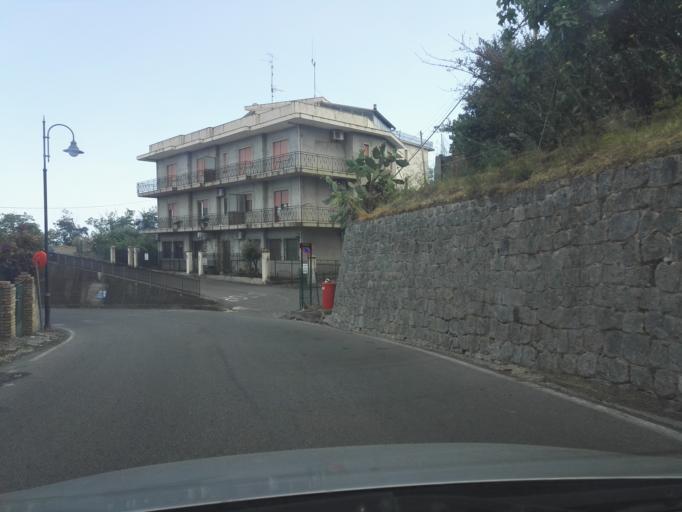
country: IT
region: Calabria
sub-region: Provincia di Reggio Calabria
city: Riace
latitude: 38.4174
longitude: 16.4807
